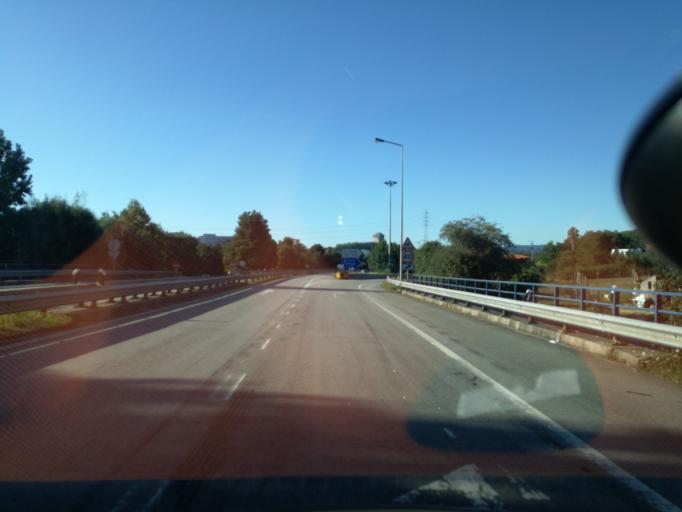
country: PT
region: Porto
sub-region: Santo Tirso
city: Sao Miguel do Couto
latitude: 41.3271
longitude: -8.4704
